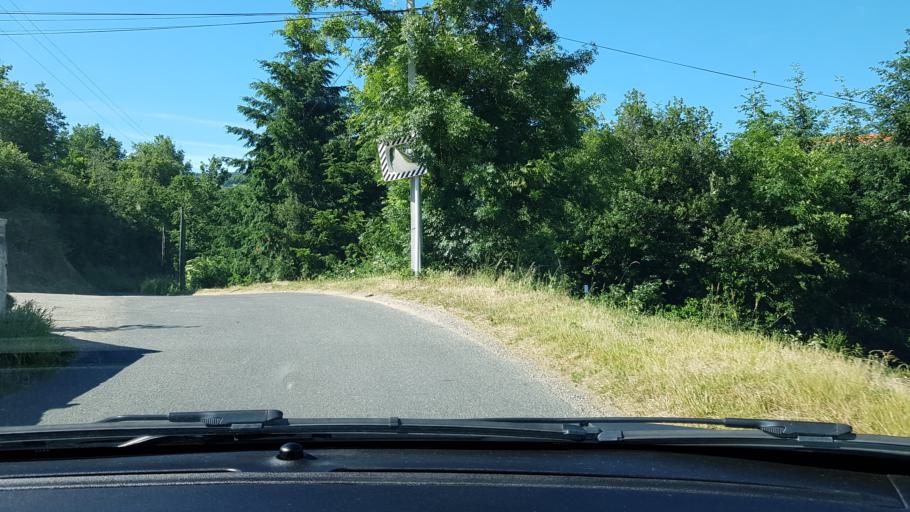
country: FR
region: Rhone-Alpes
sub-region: Departement du Rhone
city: Saint-Didier-sous-Riverie
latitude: 45.5937
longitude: 4.6064
